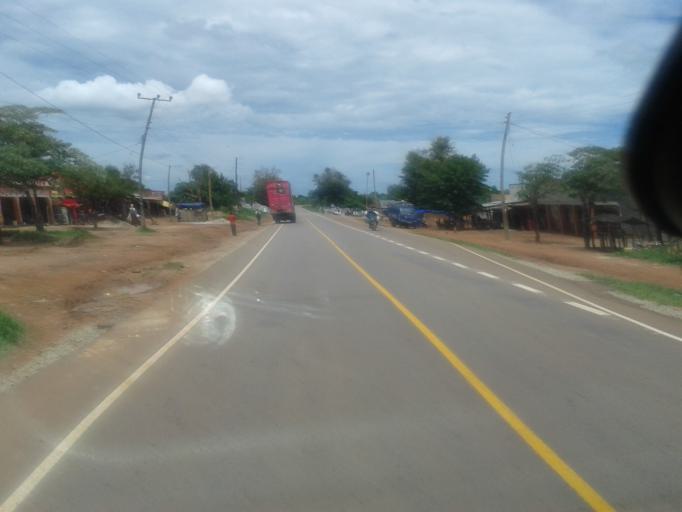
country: UG
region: Western Region
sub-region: Kiryandongo District
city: Masindi Port
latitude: 1.7114
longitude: 32.0283
